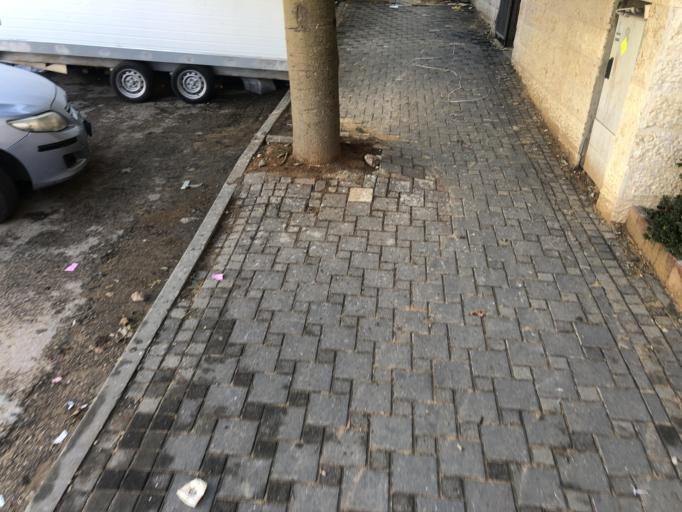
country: IL
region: Jerusalem
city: Modiin Ilit
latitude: 31.9239
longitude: 35.0489
